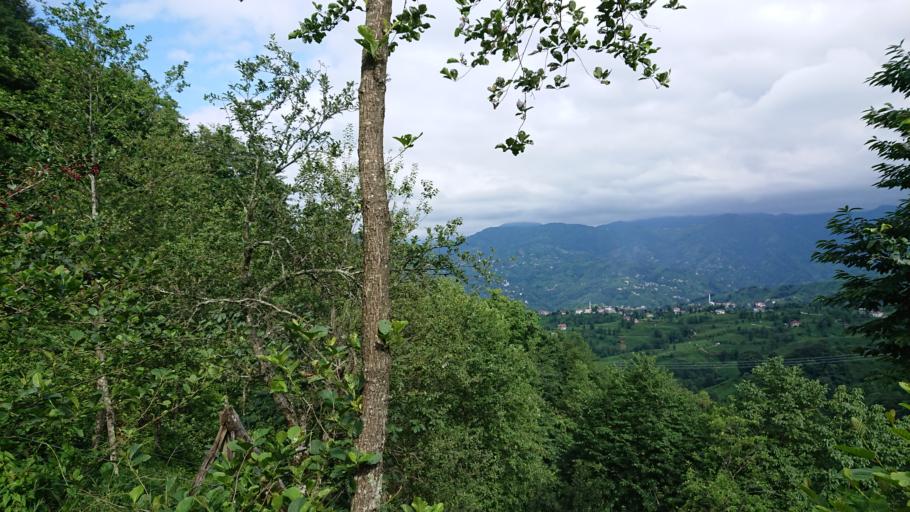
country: TR
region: Rize
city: Rize
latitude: 40.9753
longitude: 40.4983
